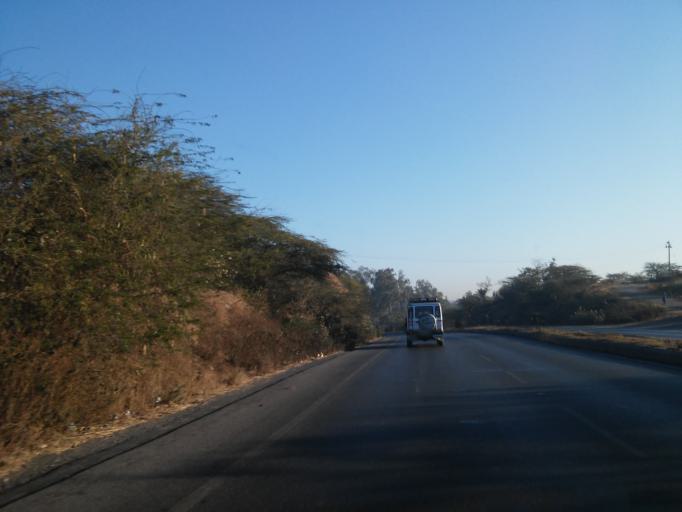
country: IN
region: Rajasthan
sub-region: Dungarpur
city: Dungarpur
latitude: 23.8747
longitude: 73.5298
